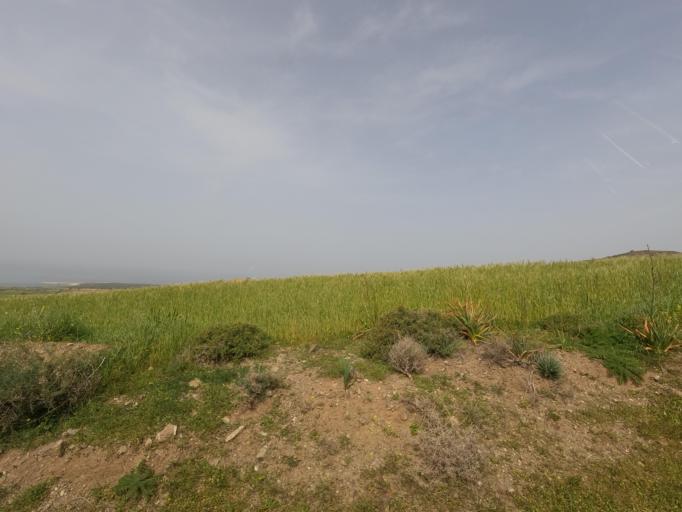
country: CY
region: Pafos
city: Pegeia
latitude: 34.9581
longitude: 32.3431
